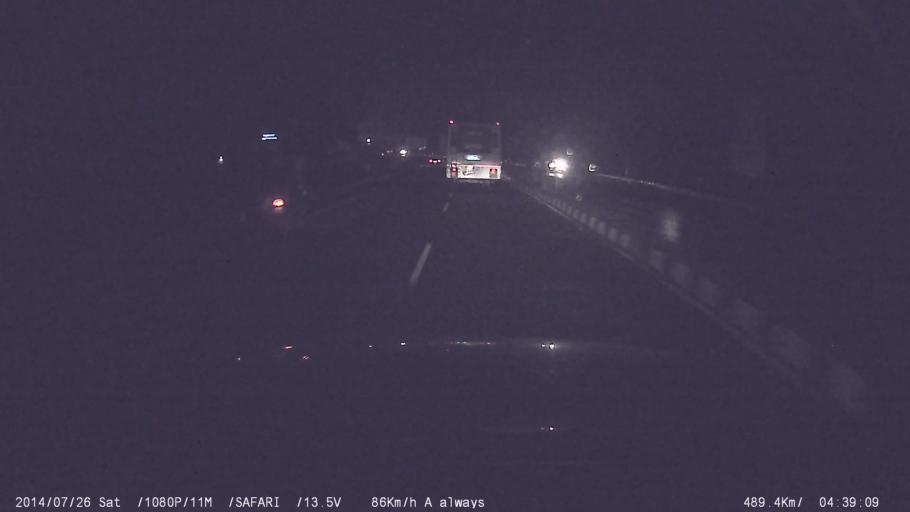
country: IN
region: Kerala
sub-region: Ernakulam
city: Angamali
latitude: 10.2357
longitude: 76.3735
